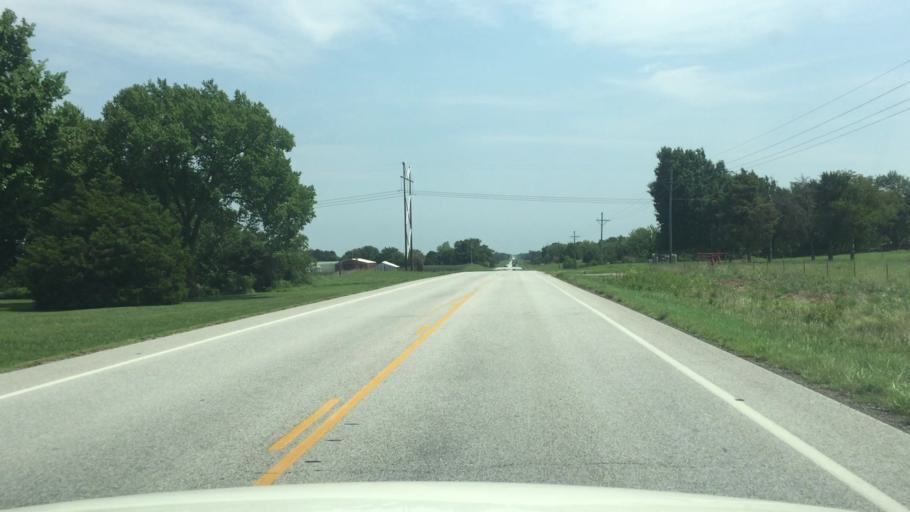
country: US
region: Kansas
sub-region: Cherokee County
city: Columbus
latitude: 37.1780
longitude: -94.7827
